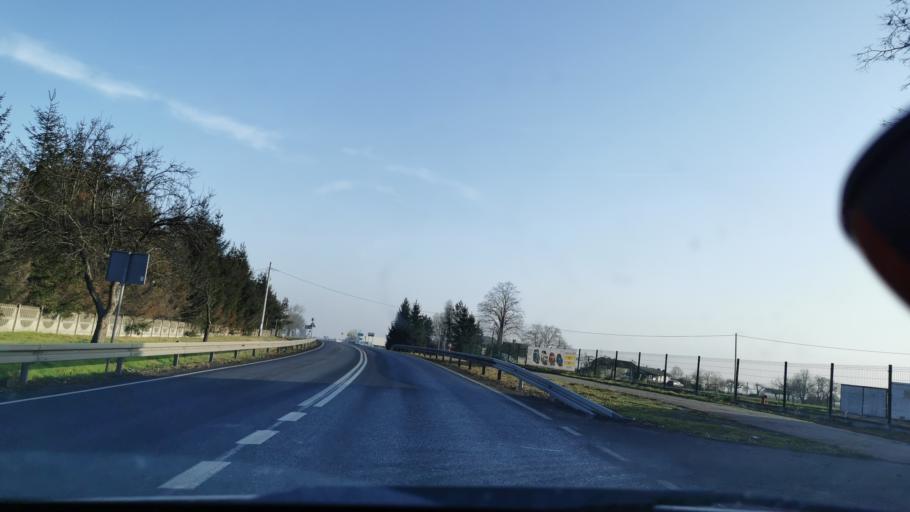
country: PL
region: Lodz Voivodeship
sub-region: Powiat sieradzki
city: Blaszki
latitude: 51.6849
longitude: 18.3305
